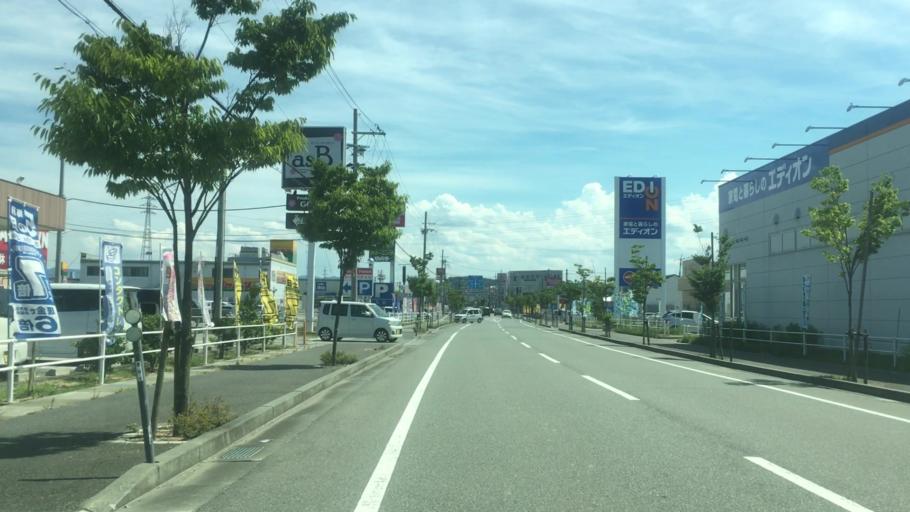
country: JP
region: Hyogo
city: Toyooka
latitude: 35.5562
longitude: 134.8156
